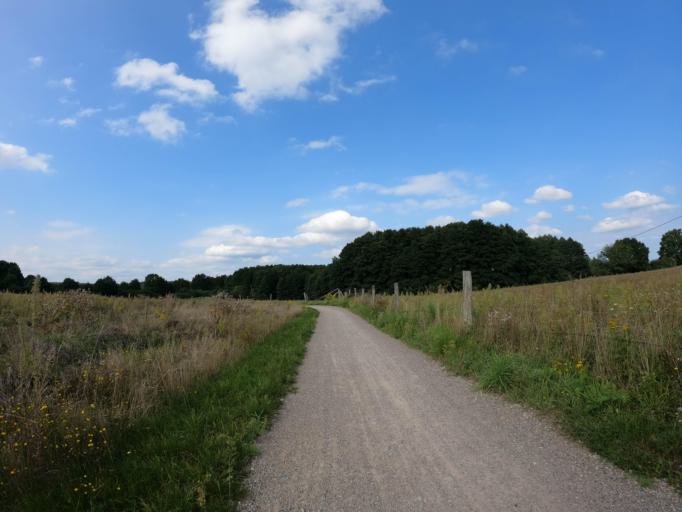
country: DE
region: Mecklenburg-Vorpommern
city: Malchow
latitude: 53.4958
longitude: 12.4330
